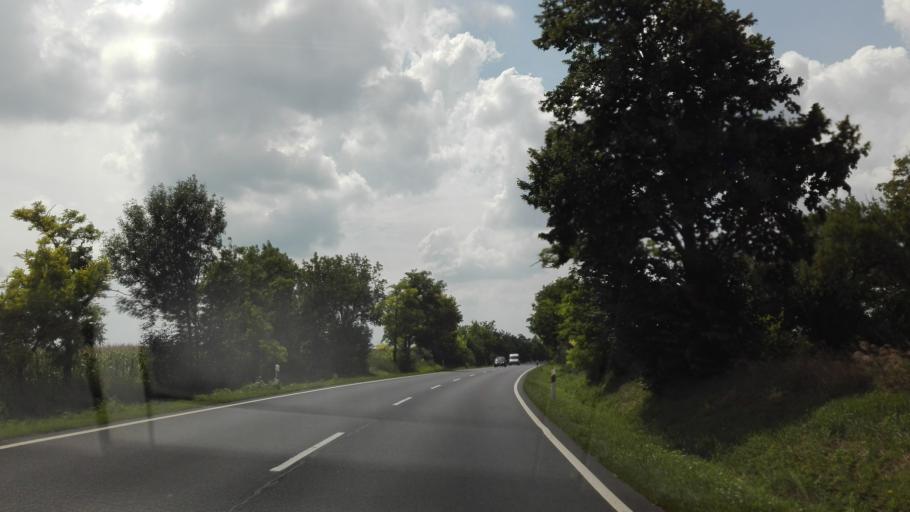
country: HU
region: Fejer
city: Eloszallas
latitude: 46.8057
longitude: 18.7652
